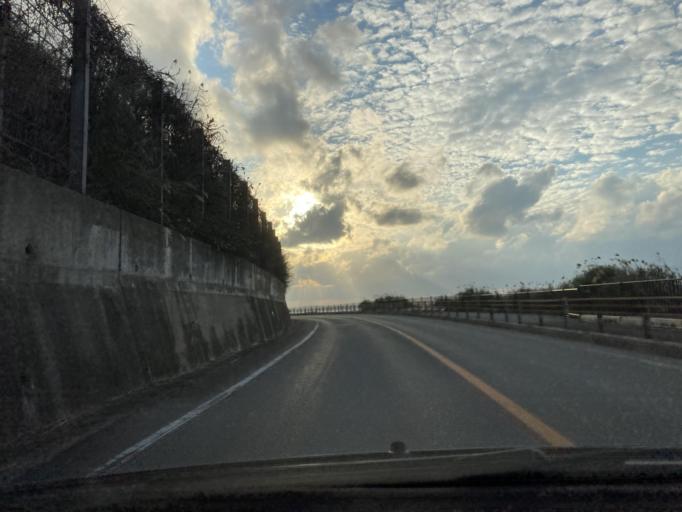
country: JP
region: Okinawa
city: Nago
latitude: 26.7970
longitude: 128.2268
